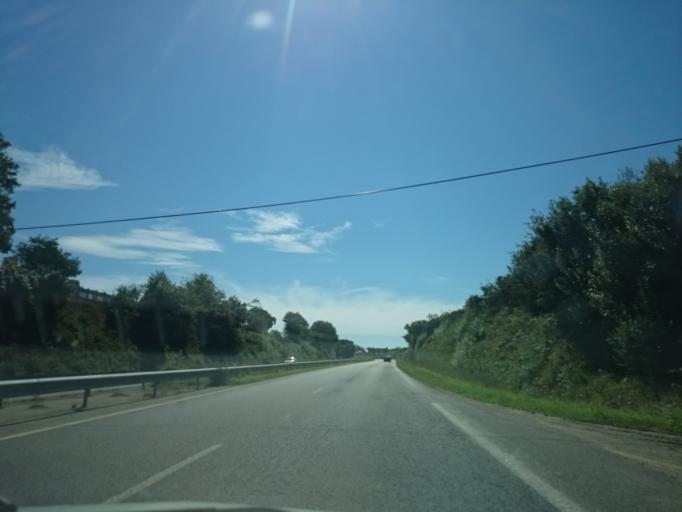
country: FR
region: Brittany
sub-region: Departement du Finistere
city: Guilers
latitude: 48.4221
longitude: -4.5664
